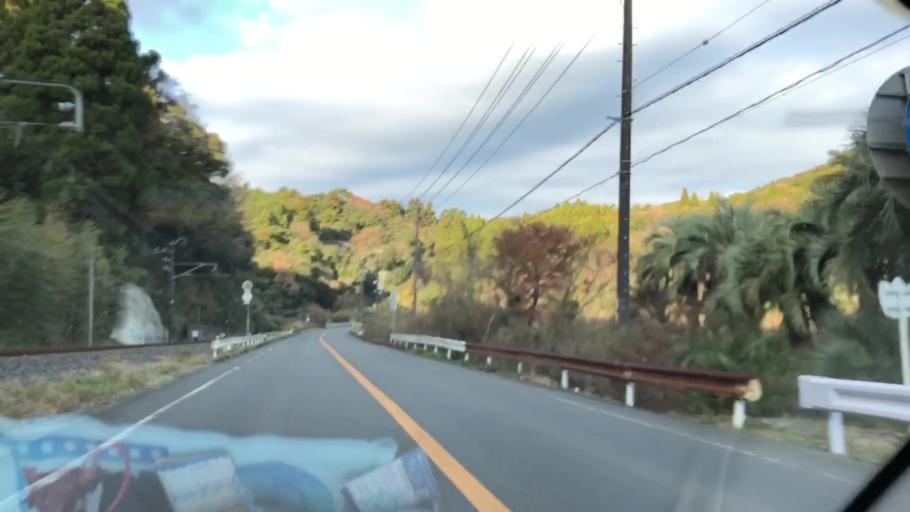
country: JP
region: Chiba
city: Tateyama
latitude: 34.9869
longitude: 139.9344
